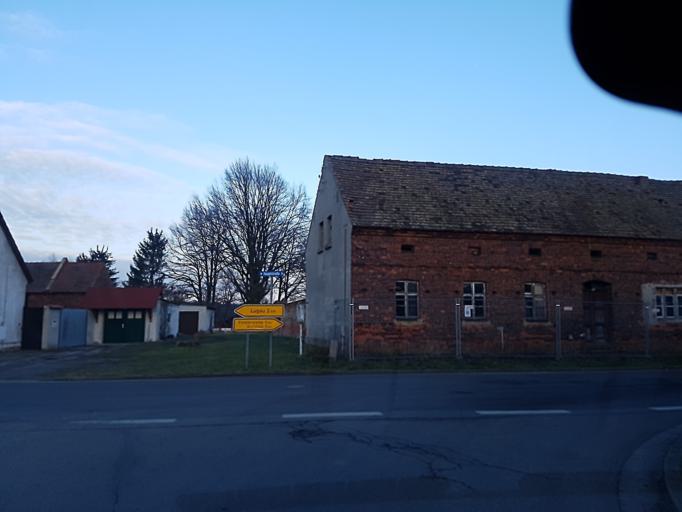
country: DE
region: Brandenburg
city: Ruckersdorf
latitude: 51.5964
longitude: 13.6081
